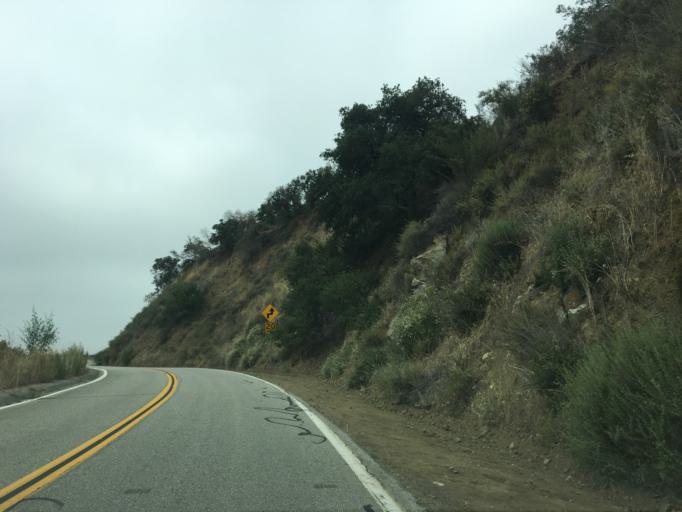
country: US
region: California
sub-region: Los Angeles County
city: Glendora
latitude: 34.1650
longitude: -117.8399
